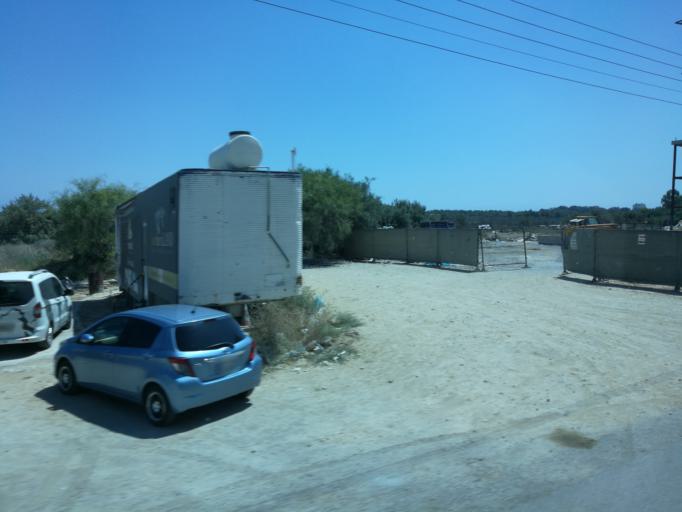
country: CY
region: Ammochostos
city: Famagusta
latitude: 35.1459
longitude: 33.9113
